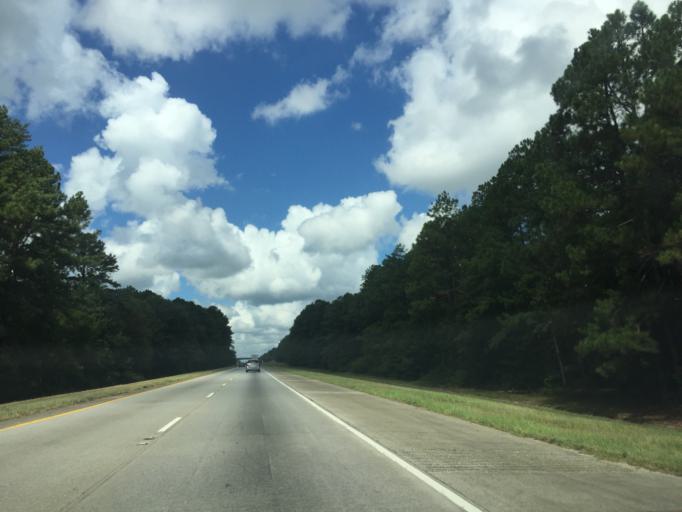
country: US
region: Georgia
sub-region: Toombs County
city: Lyons
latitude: 32.3869
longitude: -82.2596
